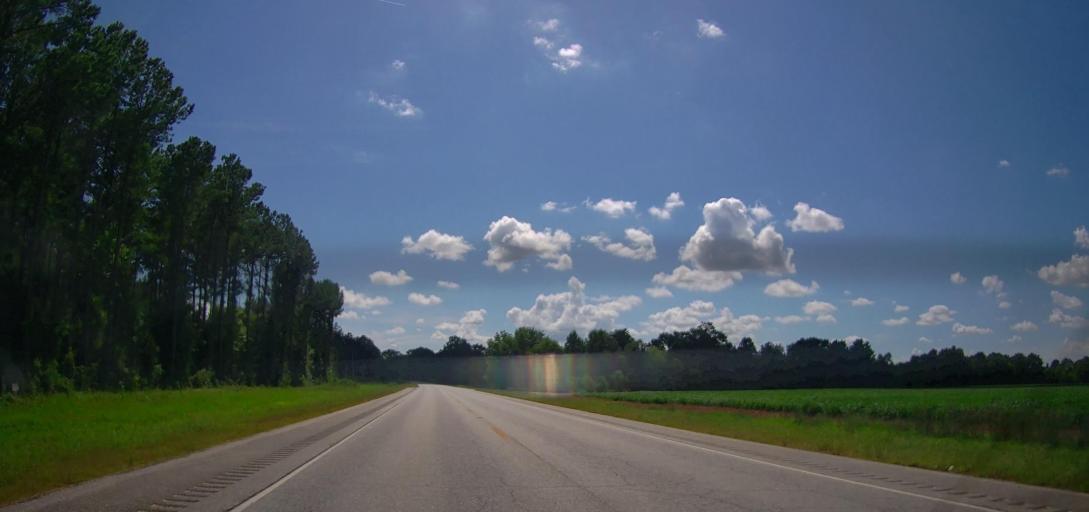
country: US
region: Alabama
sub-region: Elmore County
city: Tallassee
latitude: 32.3982
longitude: -85.9648
